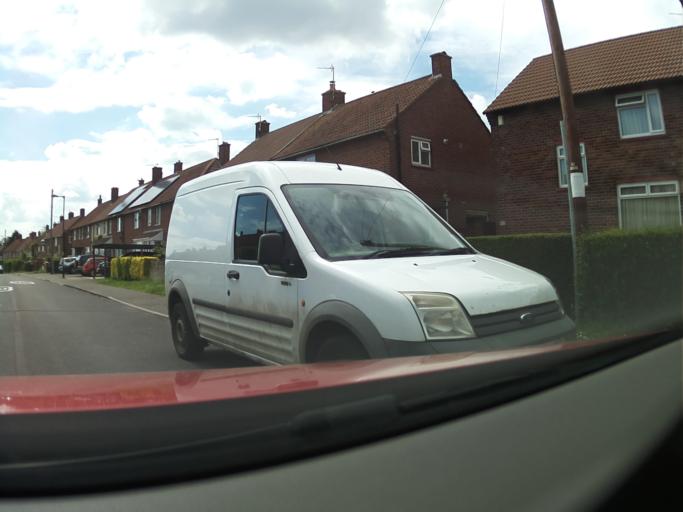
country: GB
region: England
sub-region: Bristol
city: Bristol
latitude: 51.5053
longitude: -2.6076
